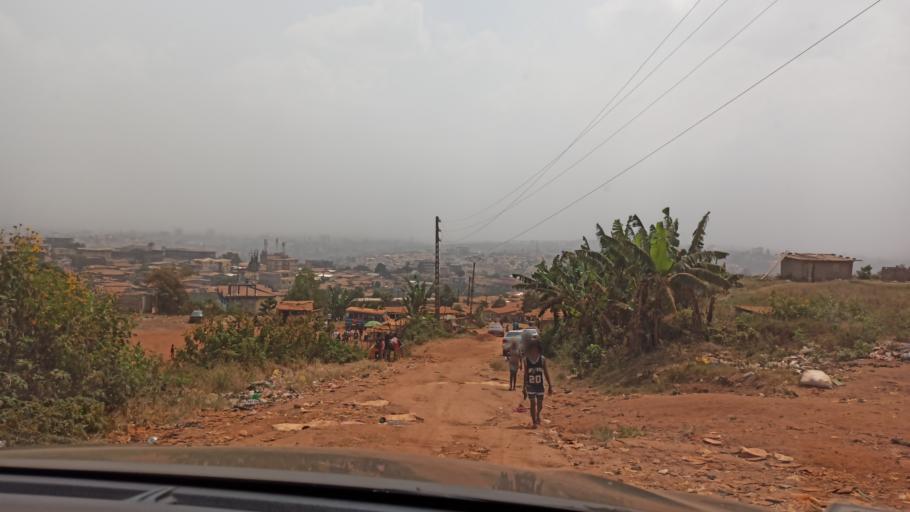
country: CM
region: Centre
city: Yaounde
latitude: 3.8864
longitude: 11.4875
